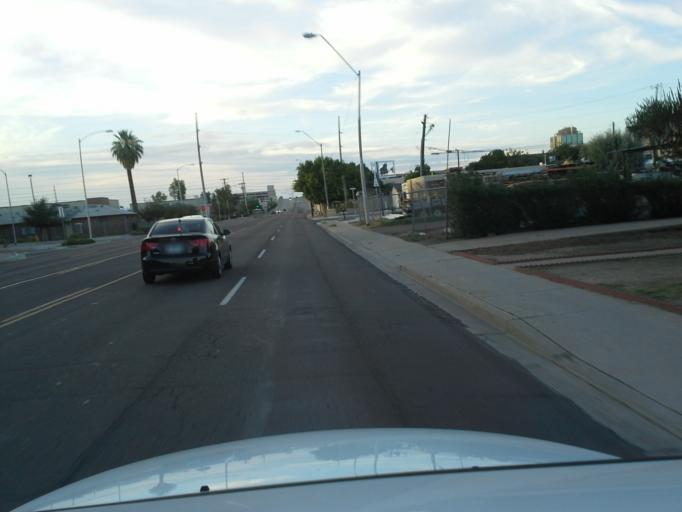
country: US
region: Arizona
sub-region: Maricopa County
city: Phoenix
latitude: 33.4384
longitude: -112.0825
